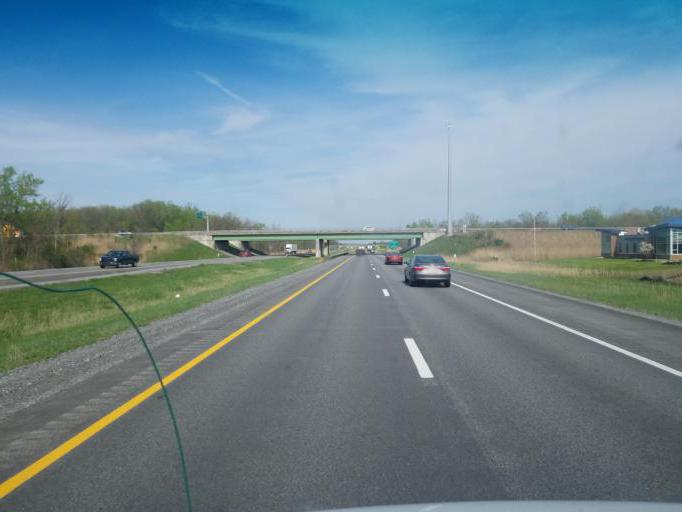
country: US
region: New York
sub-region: Onondaga County
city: East Syracuse
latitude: 43.0944
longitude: -76.0558
